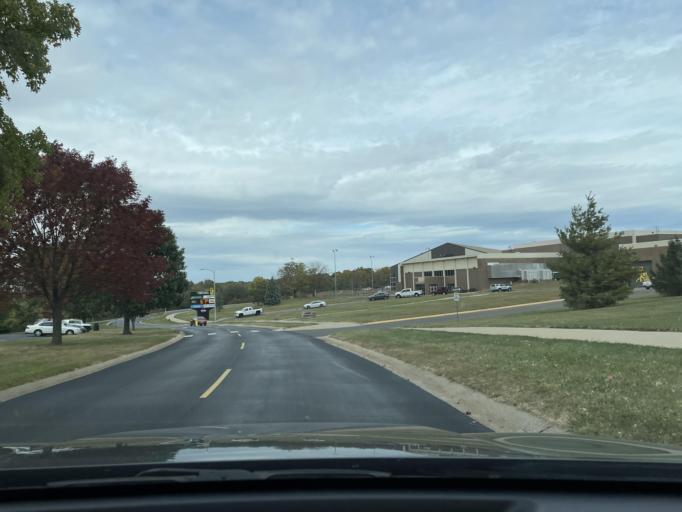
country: US
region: Missouri
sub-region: Buchanan County
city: Saint Joseph
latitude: 39.7587
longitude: -94.7893
